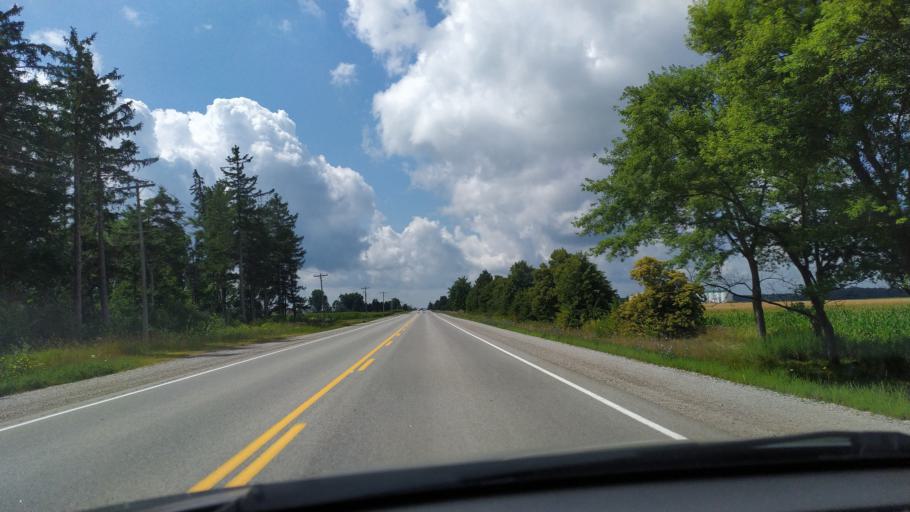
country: CA
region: Ontario
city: Huron East
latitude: 43.4177
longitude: -81.2409
